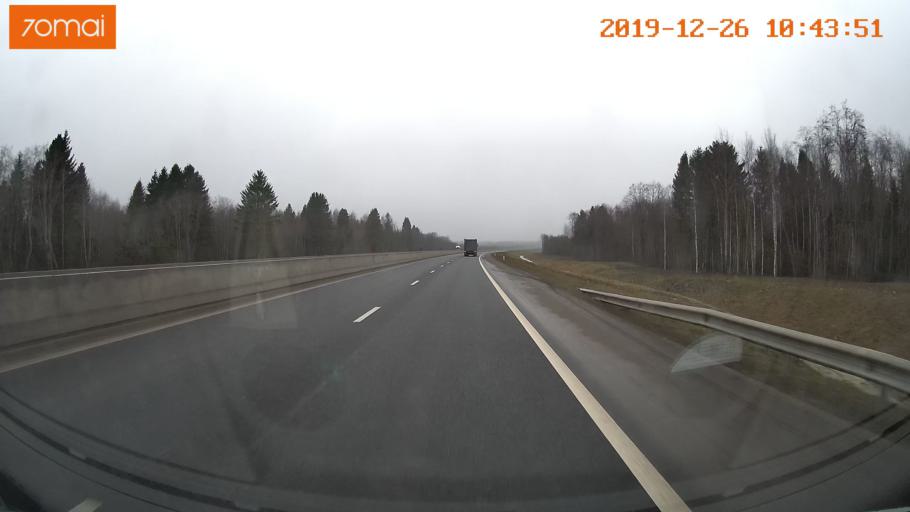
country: RU
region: Vologda
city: Vologda
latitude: 59.1704
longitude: 39.7753
